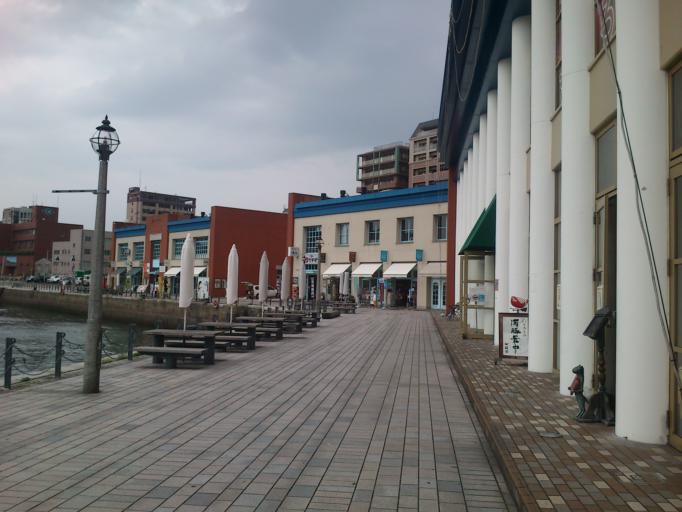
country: JP
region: Yamaguchi
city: Shimonoseki
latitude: 33.9461
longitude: 130.9625
